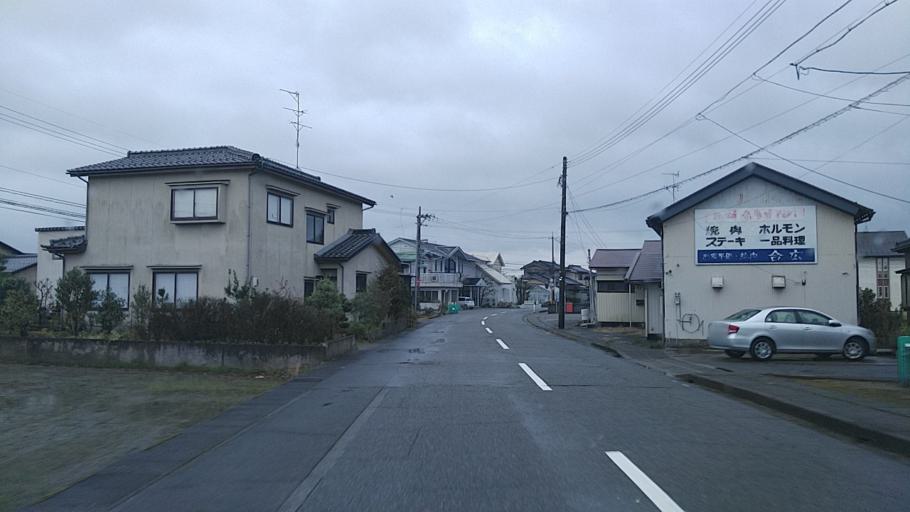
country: JP
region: Ishikawa
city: Komatsu
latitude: 36.3324
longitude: 136.3802
